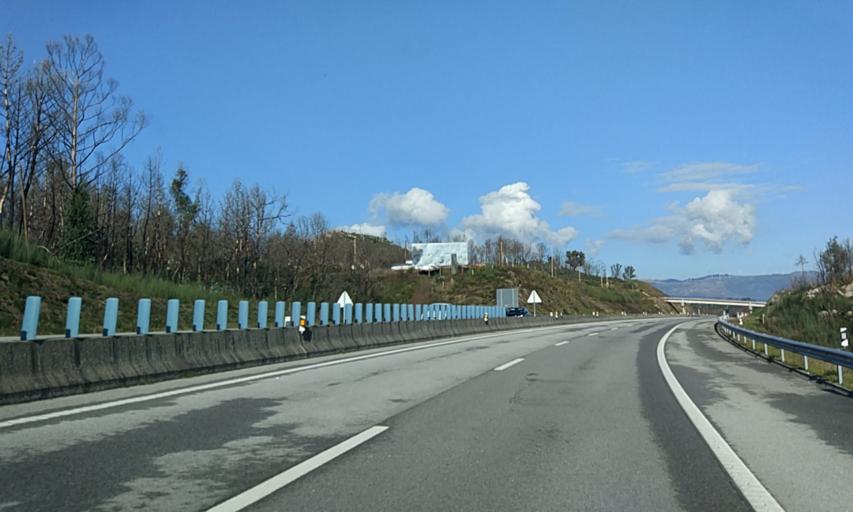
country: PT
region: Viseu
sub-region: Vouzela
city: Vouzela
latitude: 40.7020
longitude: -8.1089
